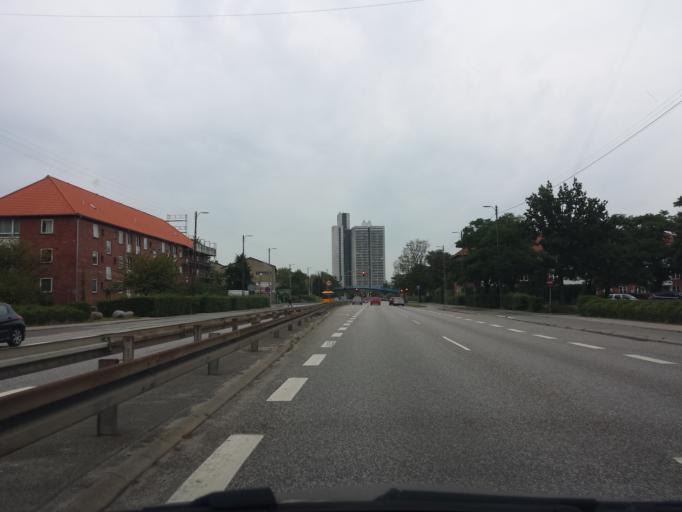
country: DK
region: Capital Region
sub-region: Herlev Kommune
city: Herlev
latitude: 55.7236
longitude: 12.4415
